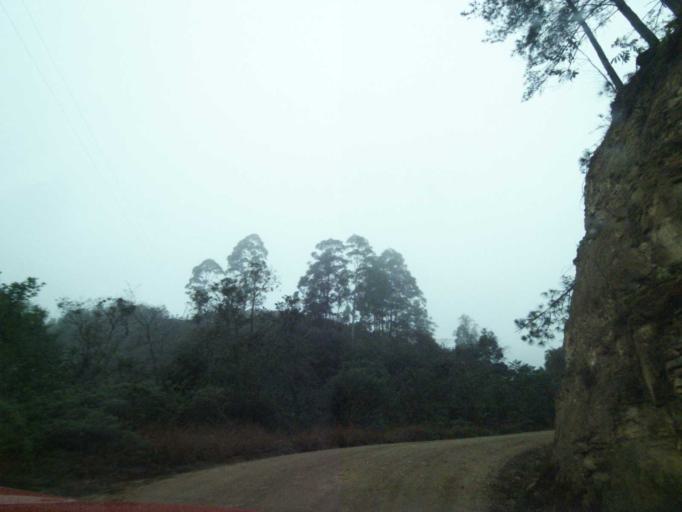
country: BR
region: Santa Catarina
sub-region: Anitapolis
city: Anitapolis
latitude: -27.9102
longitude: -49.1174
